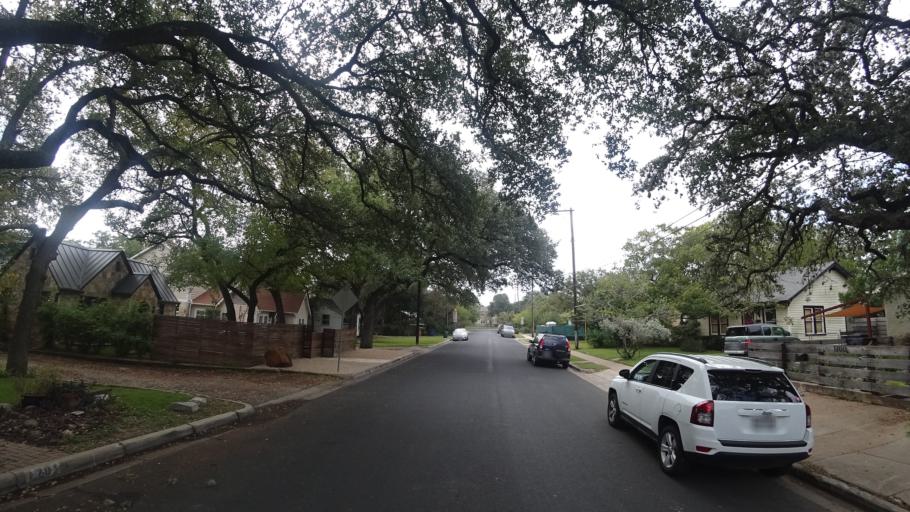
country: US
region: Texas
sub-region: Travis County
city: Austin
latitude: 30.2497
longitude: -97.7592
